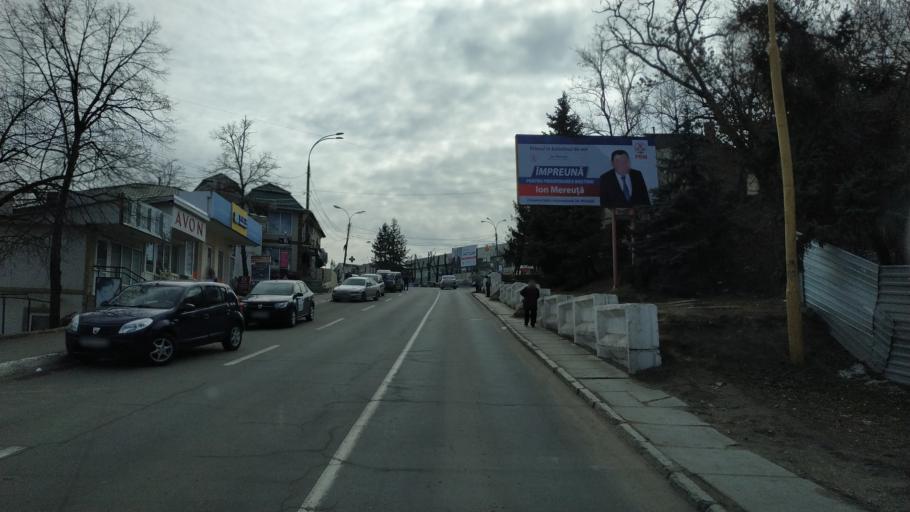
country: MD
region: Hincesti
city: Hincesti
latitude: 46.8289
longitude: 28.5887
